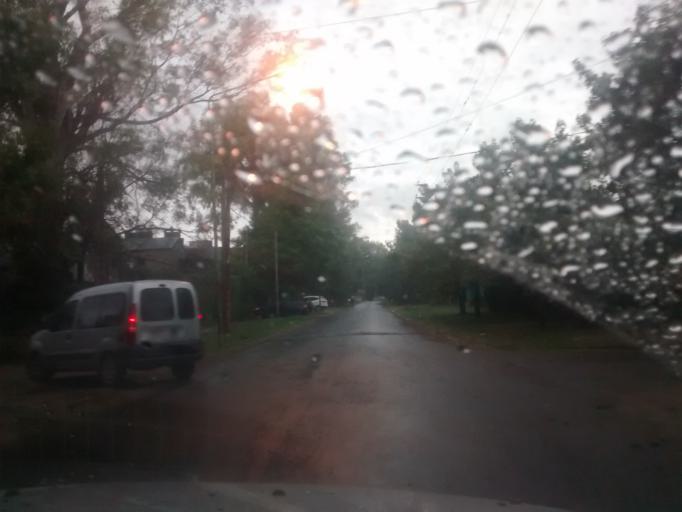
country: AR
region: Buenos Aires
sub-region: Partido de La Plata
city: La Plata
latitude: -34.8828
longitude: -58.0651
